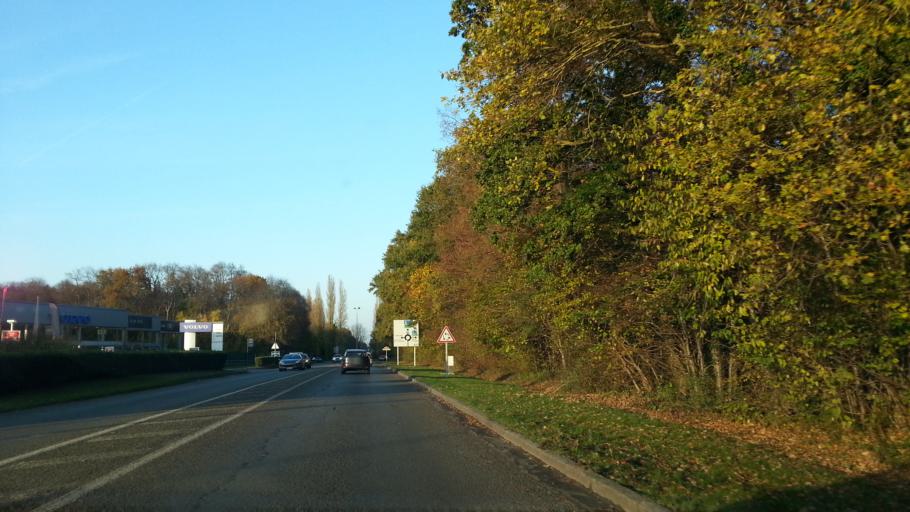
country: FR
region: Picardie
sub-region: Departement de l'Oise
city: Chantilly
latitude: 49.2033
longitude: 2.4614
